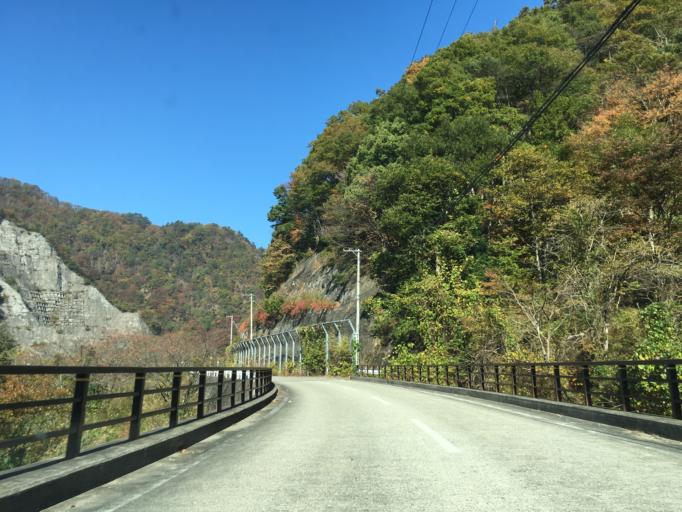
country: JP
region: Fukushima
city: Inawashiro
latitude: 37.4544
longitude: 139.9664
